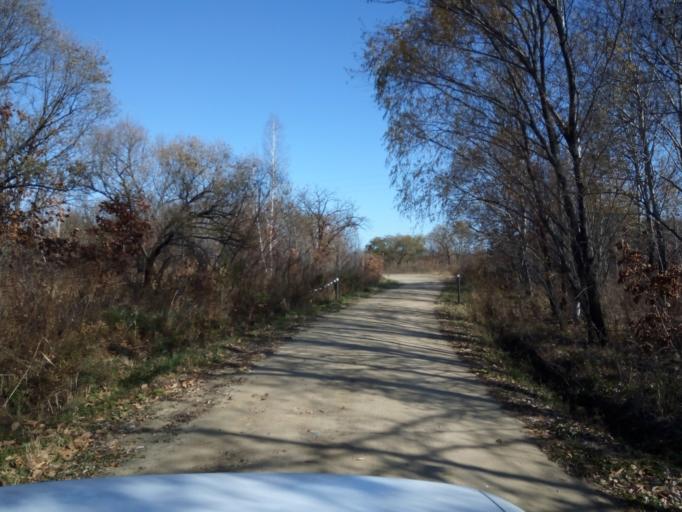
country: RU
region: Primorskiy
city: Dal'nerechensk
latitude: 45.9115
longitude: 133.8078
